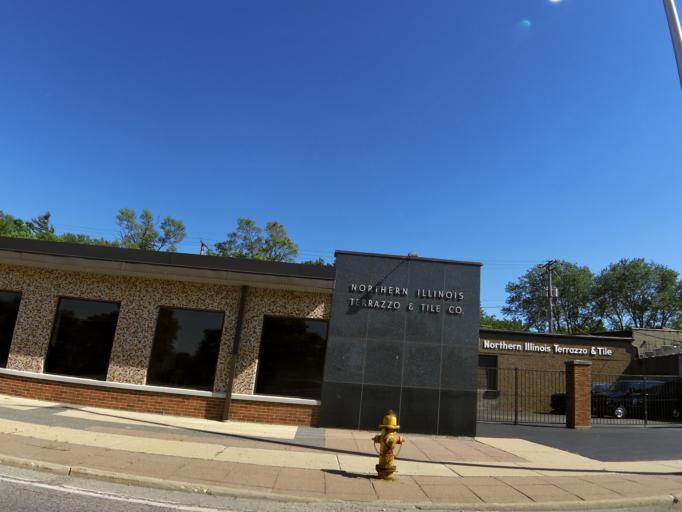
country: US
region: Illinois
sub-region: Winnebago County
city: Rockford
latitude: 42.2807
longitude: -89.0733
